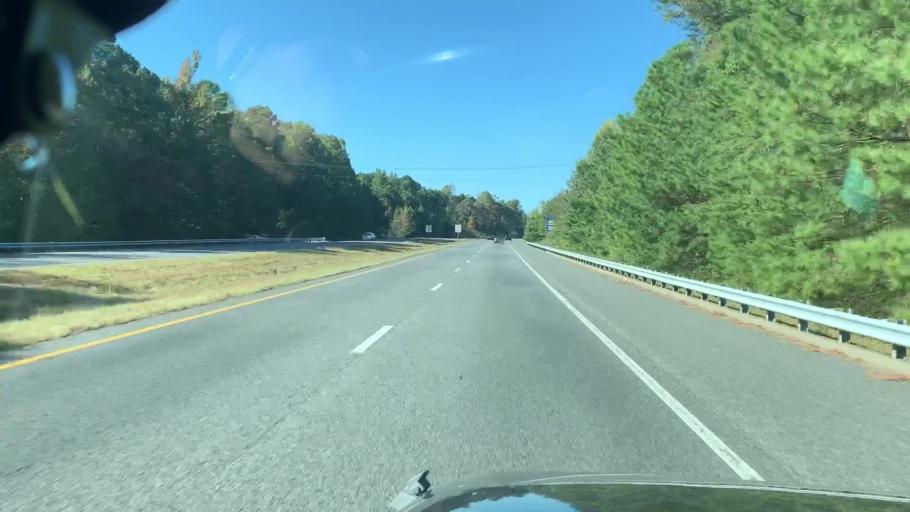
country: US
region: Virginia
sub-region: James City County
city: Williamsburg
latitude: 37.3221
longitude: -76.7523
